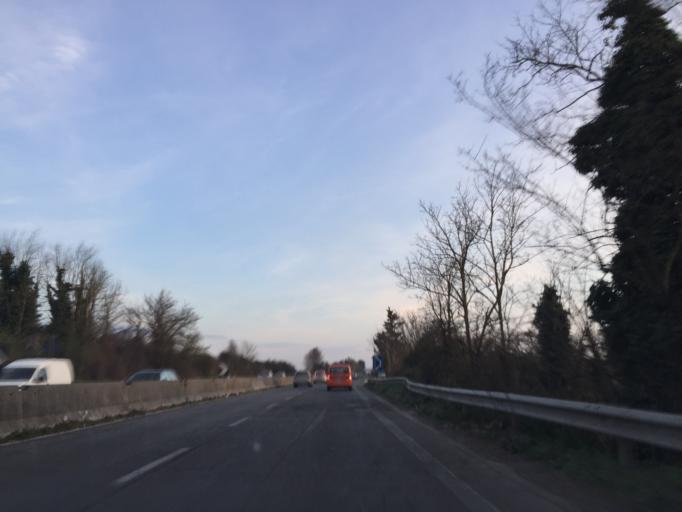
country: IT
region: Latium
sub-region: Citta metropolitana di Roma Capitale
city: Formello
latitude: 42.0295
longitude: 12.4309
